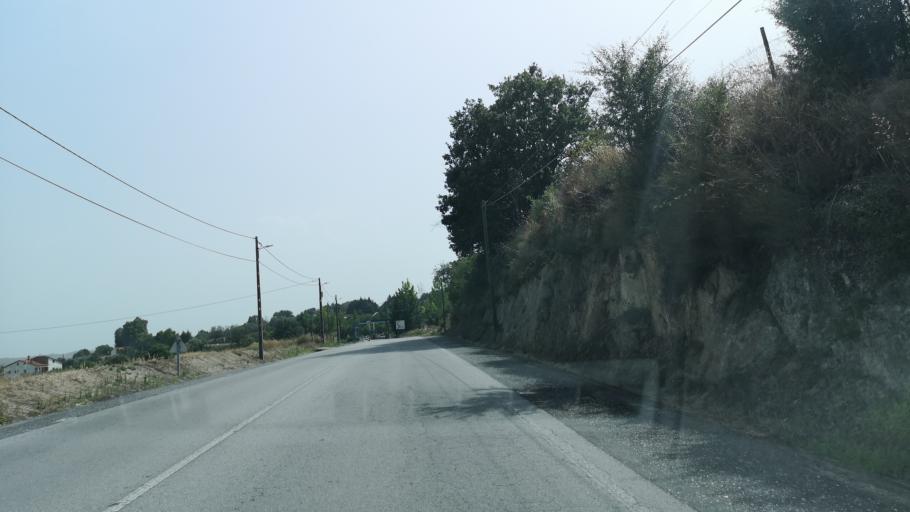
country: PT
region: Castelo Branco
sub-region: Belmonte
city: Belmonte
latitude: 40.3499
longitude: -7.3479
